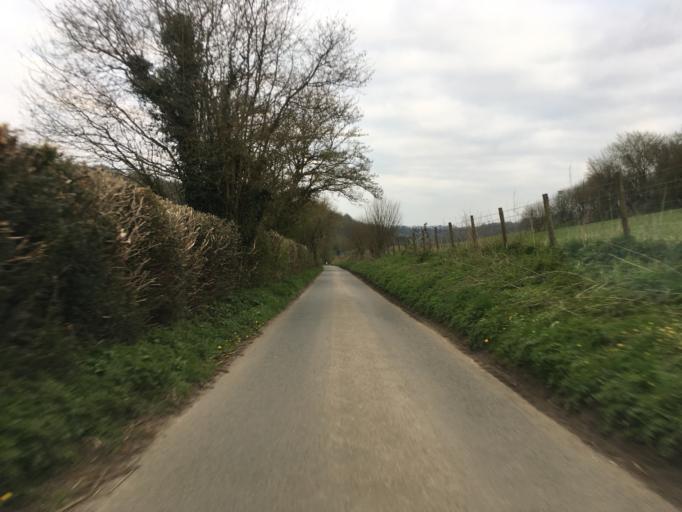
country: GB
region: England
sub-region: Gloucestershire
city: Wotton-under-Edge
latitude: 51.6053
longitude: -2.3167
